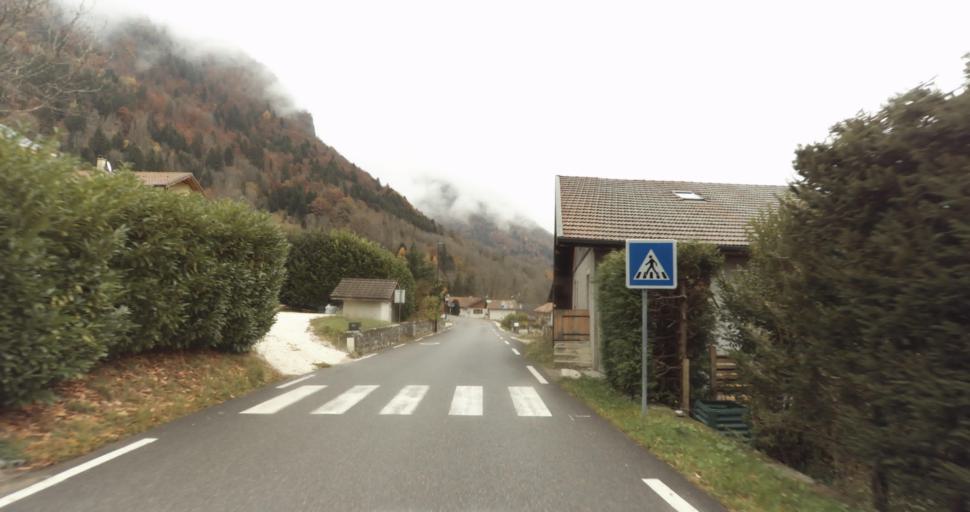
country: FR
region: Rhone-Alpes
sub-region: Departement de la Haute-Savoie
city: Thorens-Glieres
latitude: 45.9846
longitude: 6.2794
